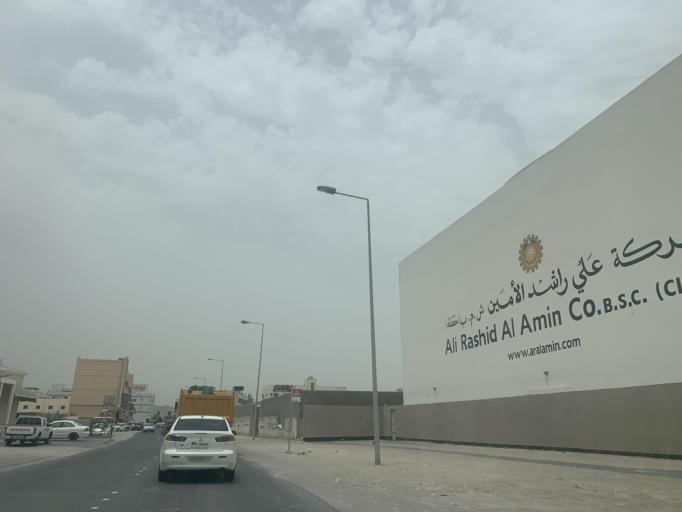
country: BH
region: Northern
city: Sitrah
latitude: 26.1720
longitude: 50.6114
